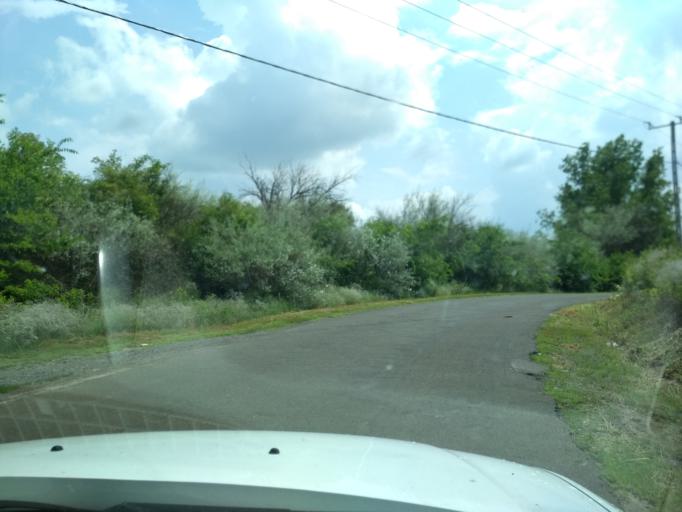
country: HU
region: Pest
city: Nagykata
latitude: 47.3813
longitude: 19.7587
